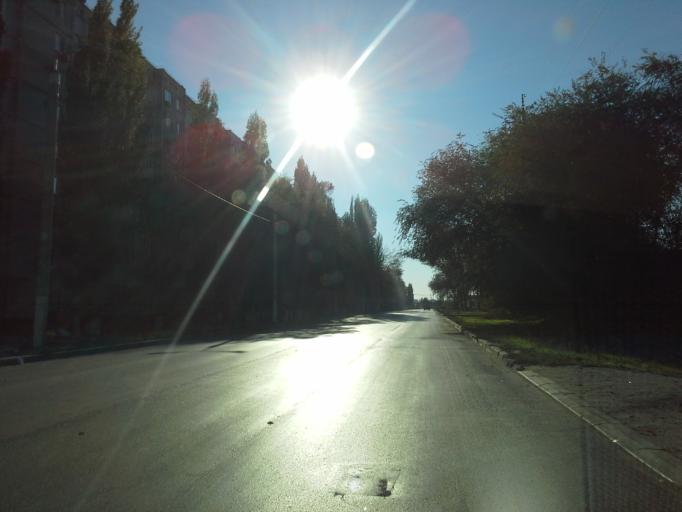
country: RU
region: Volgograd
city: Vodstroy
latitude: 48.8212
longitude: 44.6203
